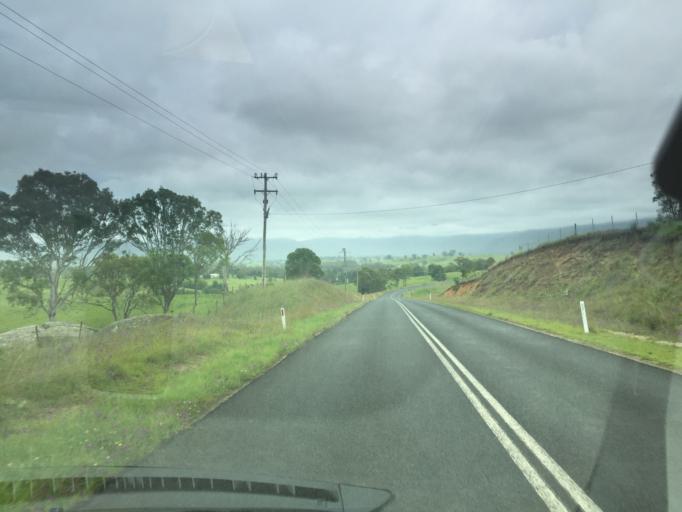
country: AU
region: New South Wales
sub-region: Bega Valley
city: Bega
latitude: -36.6508
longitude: 149.5833
